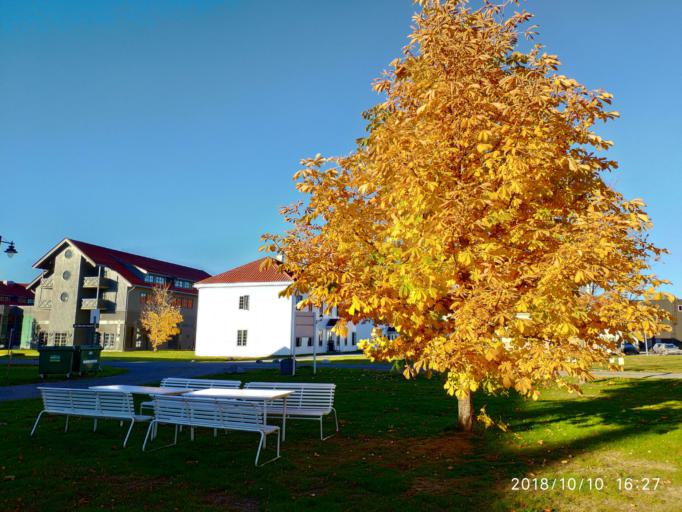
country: NO
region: Akershus
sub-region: Nannestad
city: Teigebyen
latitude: 60.1913
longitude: 11.0700
